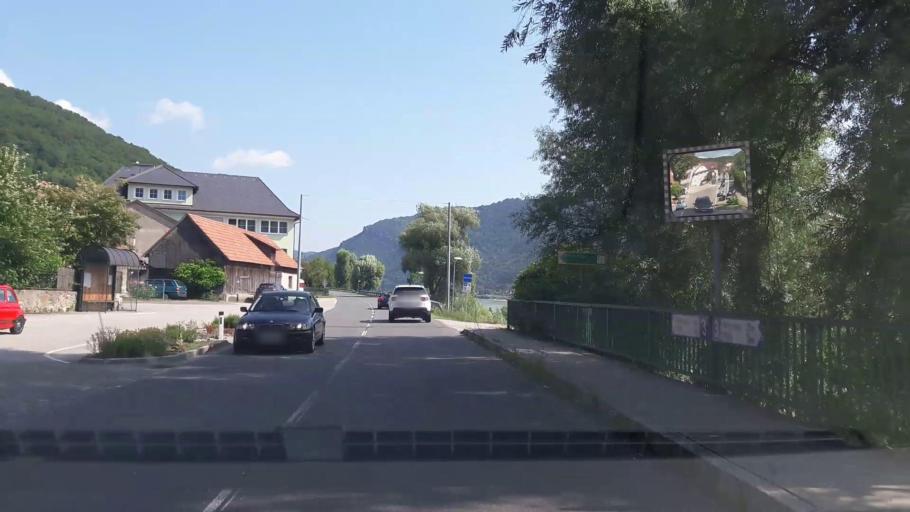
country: AT
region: Lower Austria
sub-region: Politischer Bezirk Krems
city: Aggsbach
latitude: 48.2940
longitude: 15.4044
